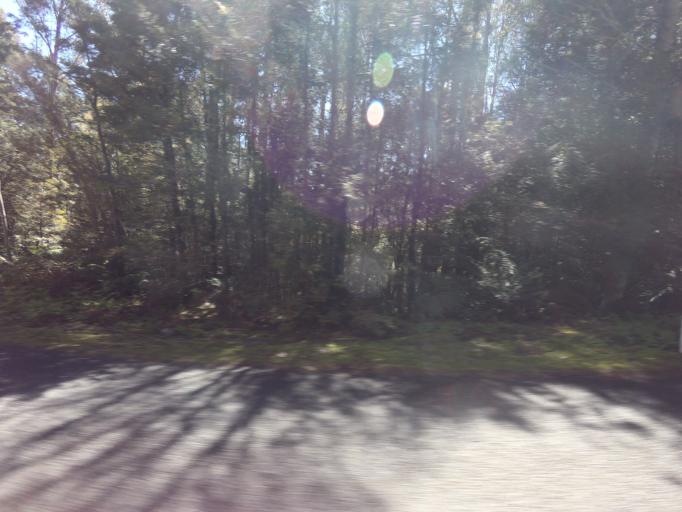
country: AU
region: Tasmania
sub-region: Huon Valley
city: Geeveston
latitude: -42.8181
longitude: 146.3566
